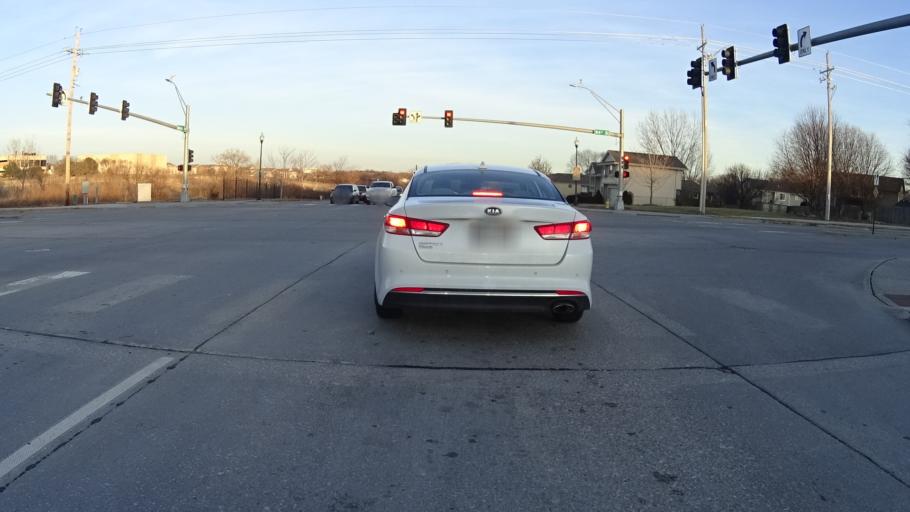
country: US
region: Nebraska
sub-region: Sarpy County
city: Papillion
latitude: 41.1326
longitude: -96.0432
